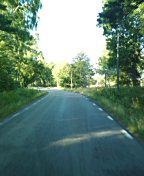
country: SE
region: Uppsala
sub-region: Habo Kommun
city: Balsta
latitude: 59.6953
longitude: 17.5355
